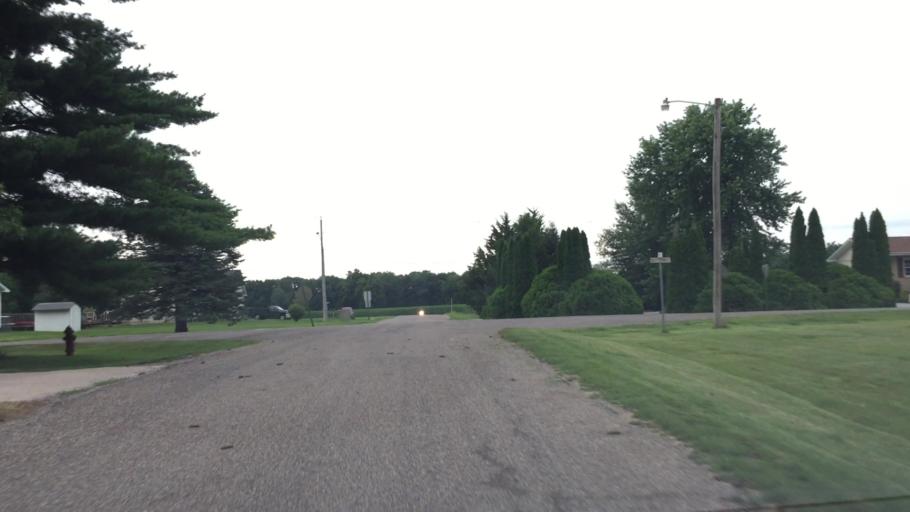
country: US
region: Illinois
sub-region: Hancock County
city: Nauvoo
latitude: 40.5322
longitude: -91.3703
